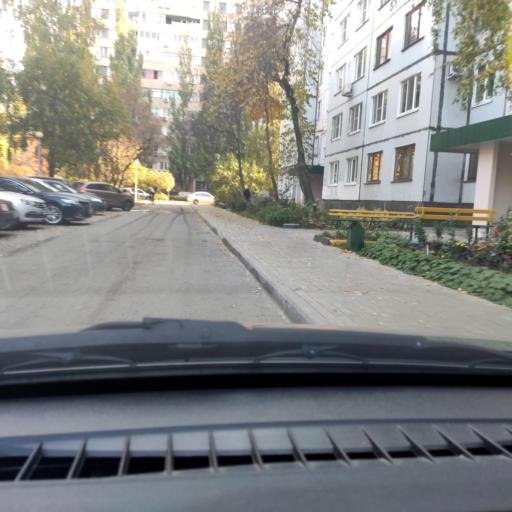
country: RU
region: Samara
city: Tol'yatti
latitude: 53.5123
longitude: 49.3017
